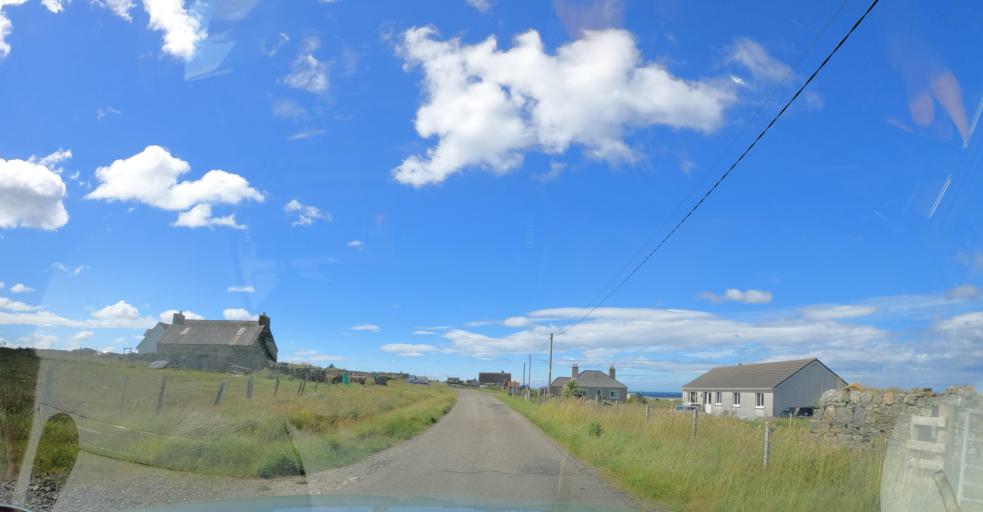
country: GB
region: Scotland
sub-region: Eilean Siar
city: Isle of Lewis
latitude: 58.3544
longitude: -6.5491
